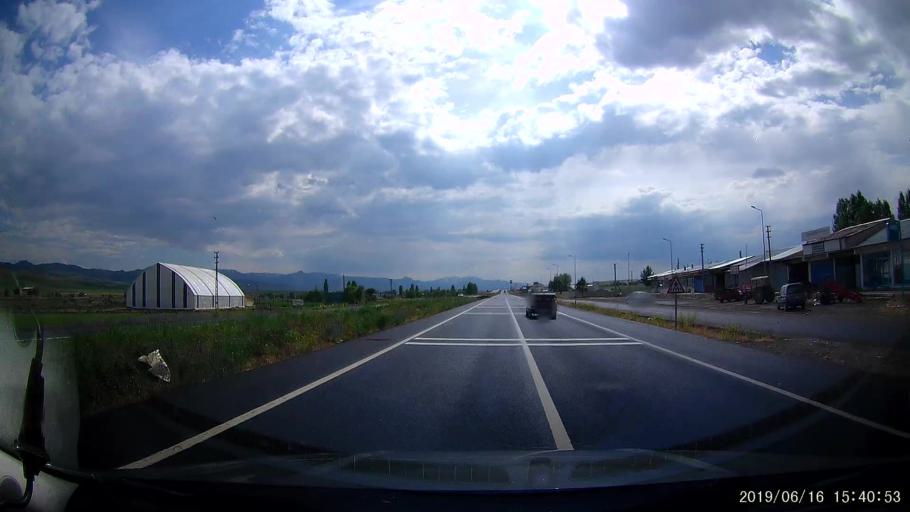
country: TR
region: Erzurum
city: Koprukoy
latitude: 39.9669
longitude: 41.8673
